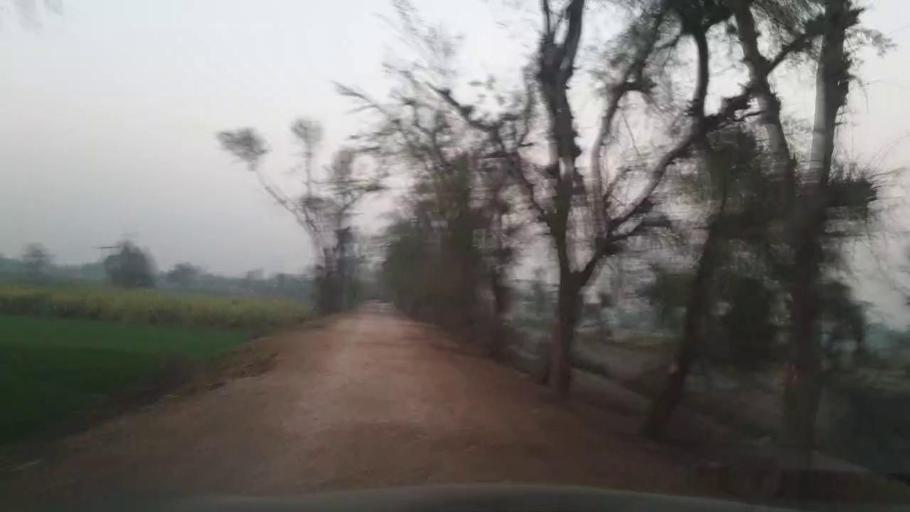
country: PK
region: Sindh
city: Ubauro
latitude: 28.1800
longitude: 69.7802
